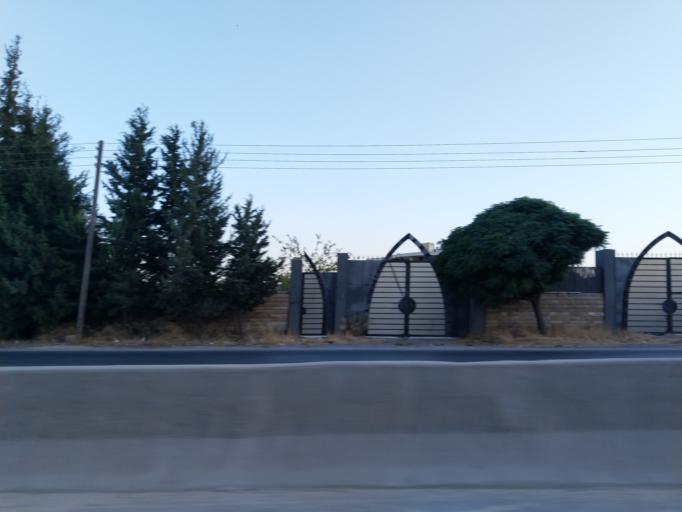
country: SY
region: Rif-dimashq
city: At Tall
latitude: 33.5858
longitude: 36.3005
